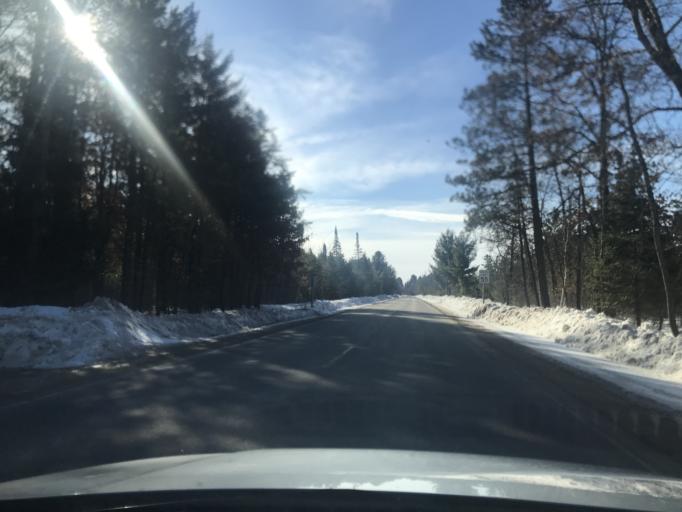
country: US
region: Wisconsin
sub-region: Marinette County
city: Niagara
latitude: 45.4194
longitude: -88.0985
